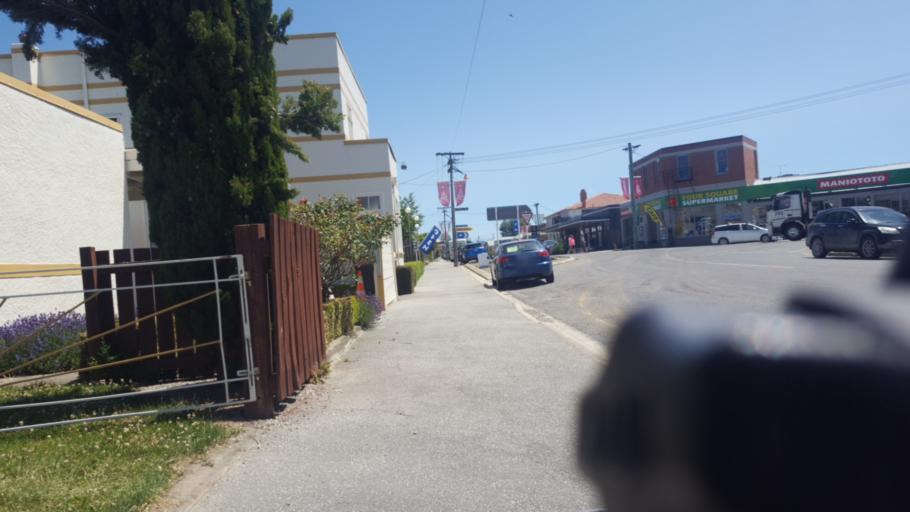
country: NZ
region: Otago
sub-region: Dunedin City
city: Dunedin
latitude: -45.1307
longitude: 170.1000
